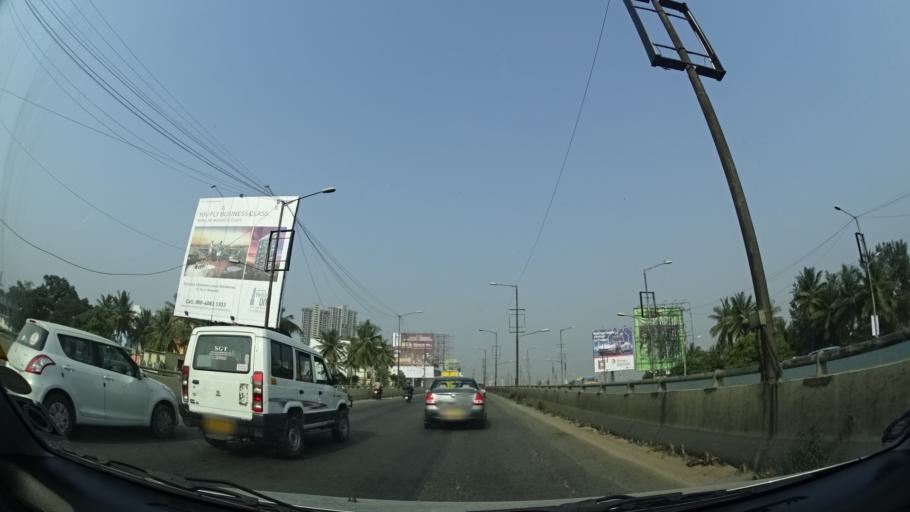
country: IN
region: Karnataka
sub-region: Bangalore Urban
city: Yelahanka
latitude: 13.0415
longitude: 77.6153
